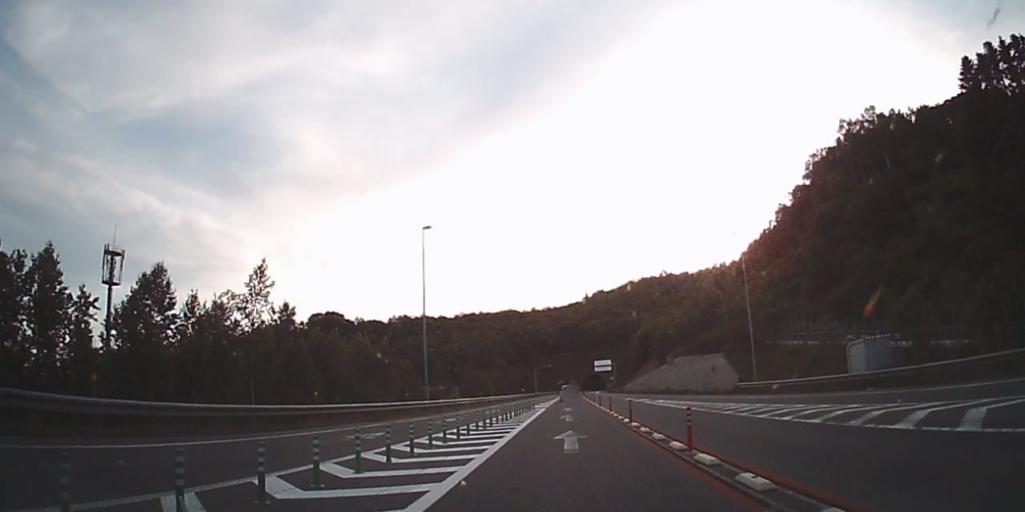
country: JP
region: Hokkaido
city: Date
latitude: 42.5582
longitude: 140.7698
